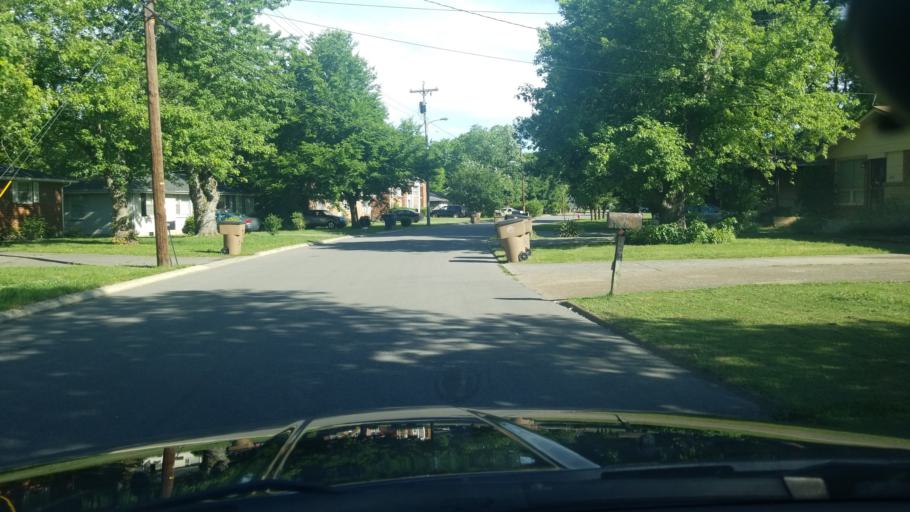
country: US
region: Tennessee
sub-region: Davidson County
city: Nashville
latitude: 36.2318
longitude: -86.7762
